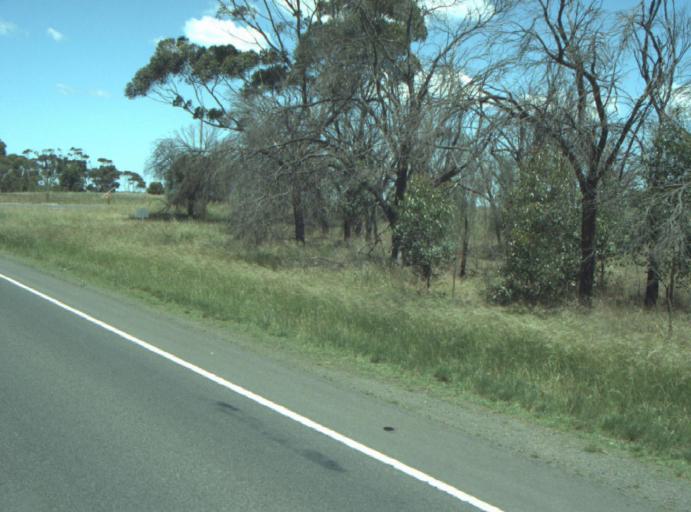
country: AU
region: Victoria
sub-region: Greater Geelong
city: Lara
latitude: -37.9583
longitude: 144.3516
